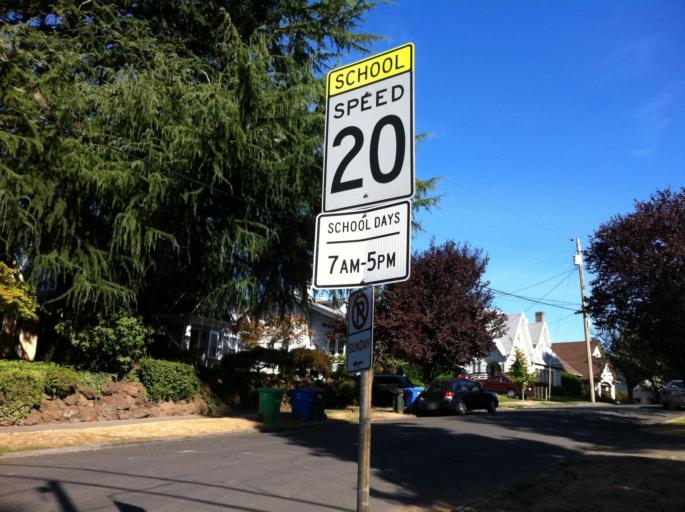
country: US
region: Oregon
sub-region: Multnomah County
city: Portland
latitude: 45.5265
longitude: -122.6250
